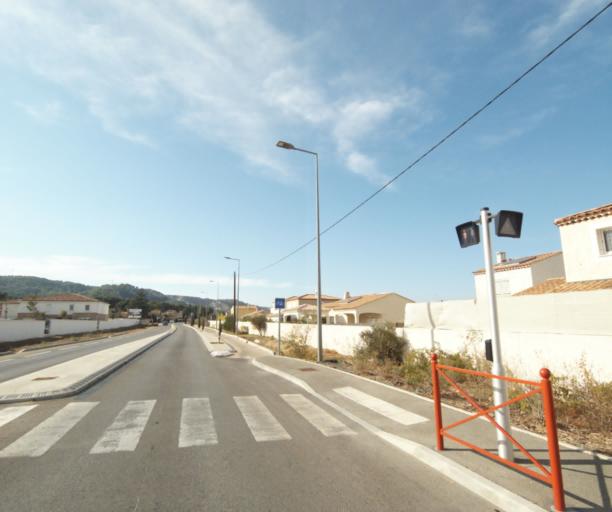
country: FR
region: Provence-Alpes-Cote d'Azur
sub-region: Departement des Bouches-du-Rhone
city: Chateauneuf-les-Martigues
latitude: 43.3806
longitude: 5.1798
